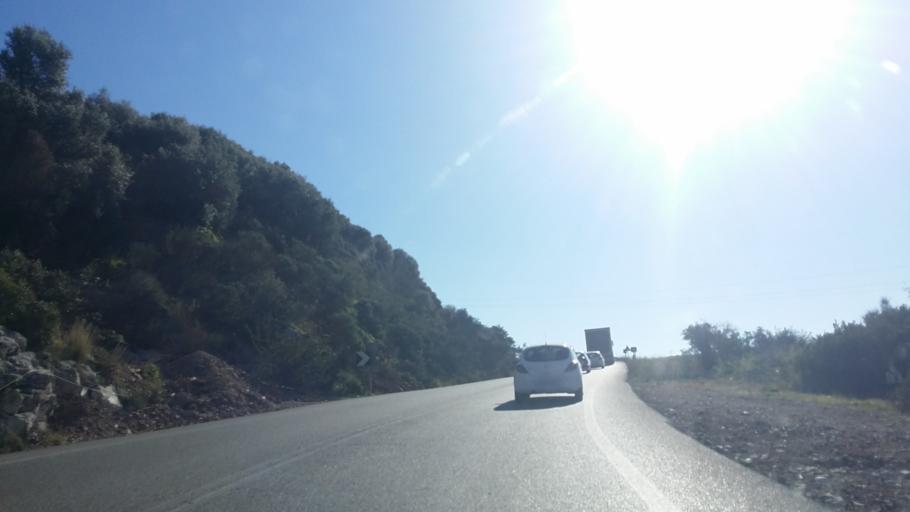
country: GR
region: West Greece
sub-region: Nomos Aitolias kai Akarnanias
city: Galatas
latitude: 38.3577
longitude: 21.6642
